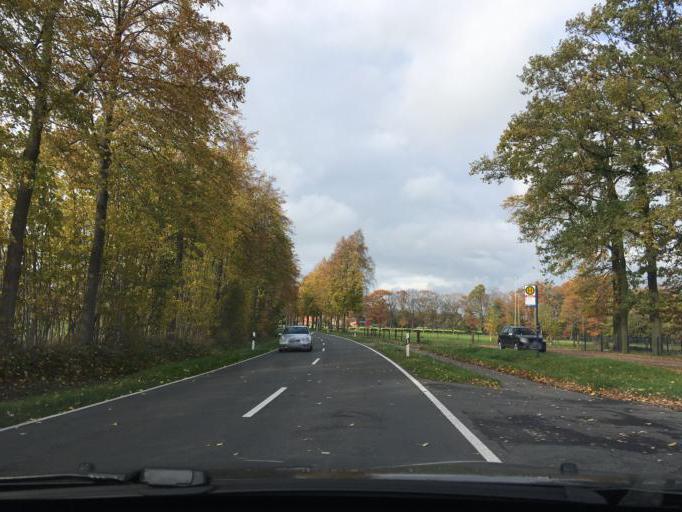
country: DE
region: North Rhine-Westphalia
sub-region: Regierungsbezirk Munster
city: Vreden
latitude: 52.0699
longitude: 6.7648
